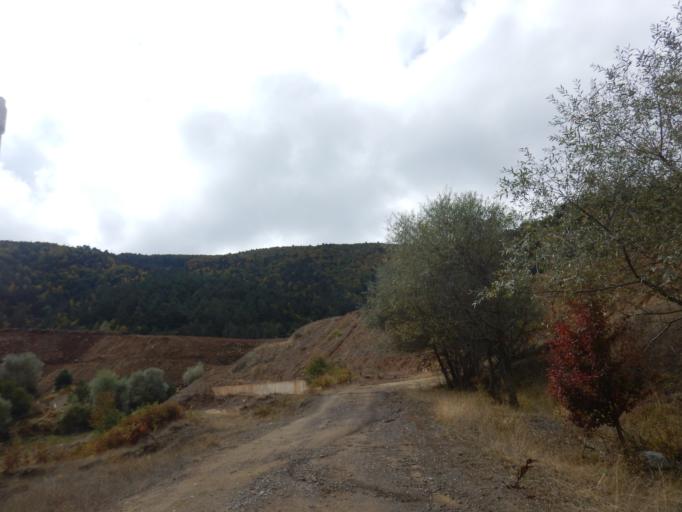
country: TR
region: Ordu
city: Mesudiye
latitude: 40.4305
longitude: 37.7804
